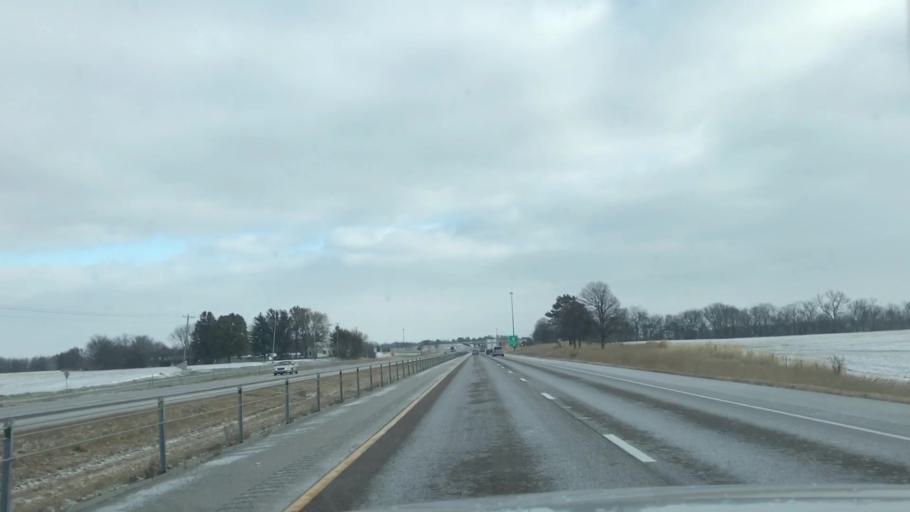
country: US
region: Illinois
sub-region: Madison County
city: Worden
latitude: 38.9249
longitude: -89.8080
